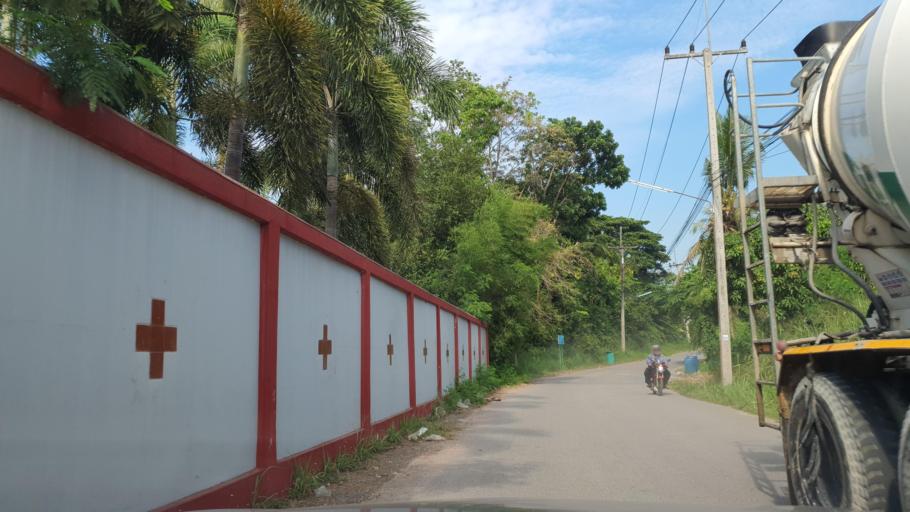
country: TH
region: Chon Buri
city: Sattahip
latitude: 12.7831
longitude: 100.9406
